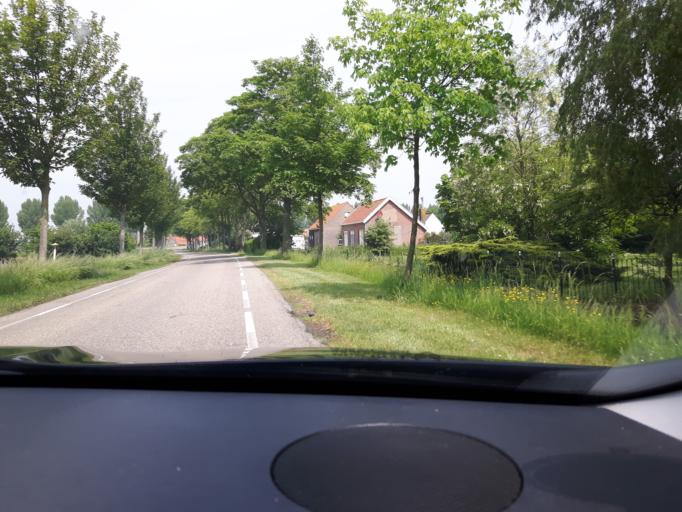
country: NL
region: Zeeland
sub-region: Gemeente Goes
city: Goes
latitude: 51.4293
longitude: 3.8791
